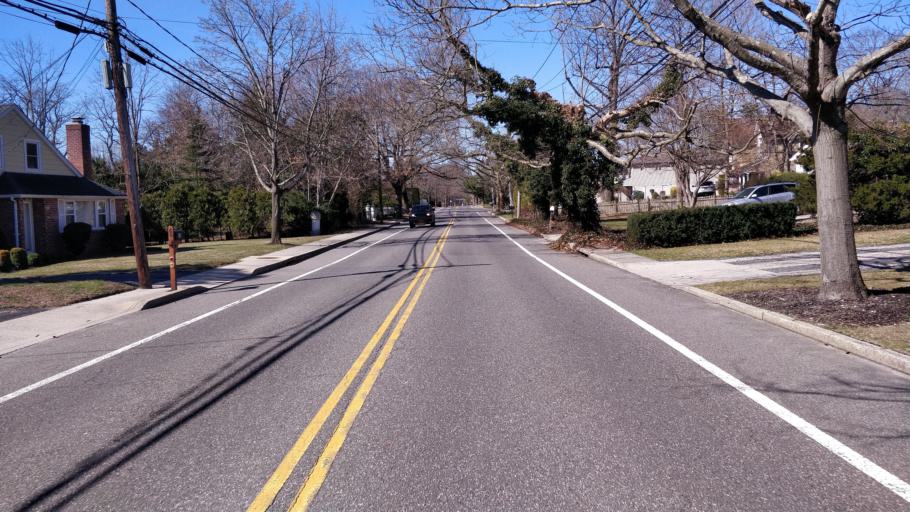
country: US
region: New York
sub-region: Suffolk County
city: Elwood
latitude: 40.8471
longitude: -73.3267
